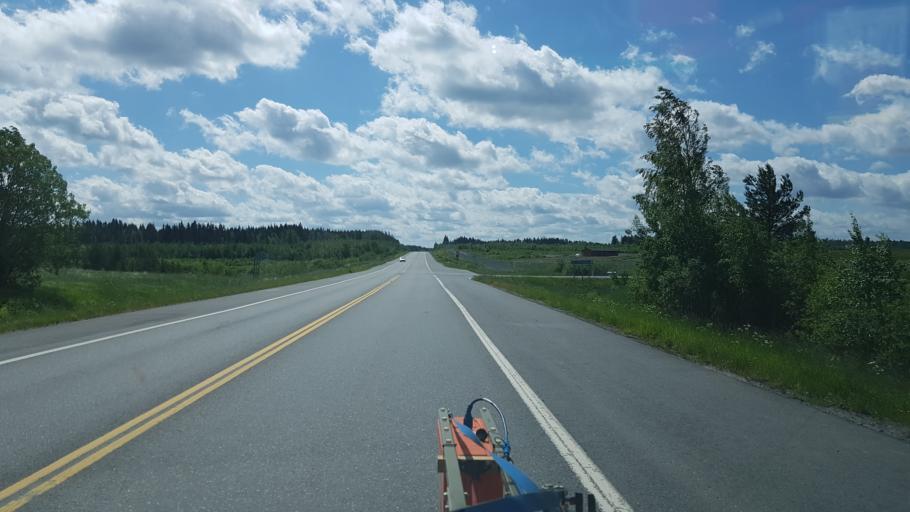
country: FI
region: Pirkanmaa
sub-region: Tampere
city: Pirkkala
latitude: 61.4231
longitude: 23.6345
